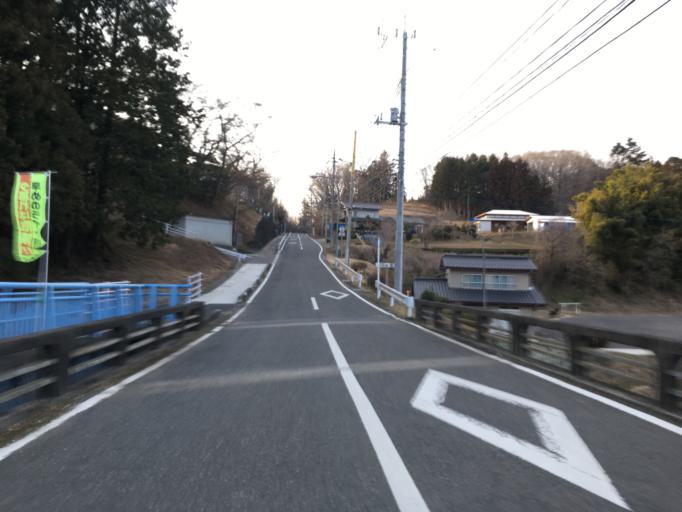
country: JP
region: Ibaraki
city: Daigo
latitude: 36.7881
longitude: 140.4188
